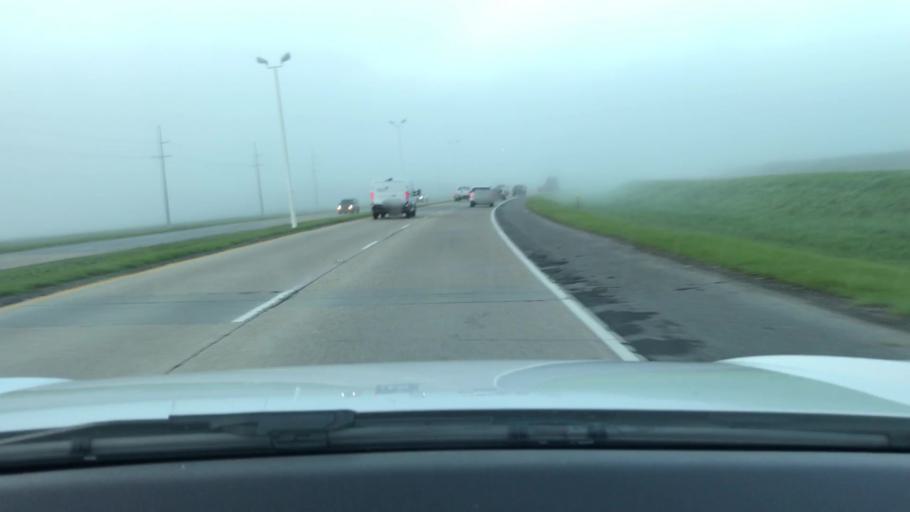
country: US
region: Louisiana
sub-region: West Baton Rouge Parish
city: Addis
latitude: 30.3508
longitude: -91.2582
